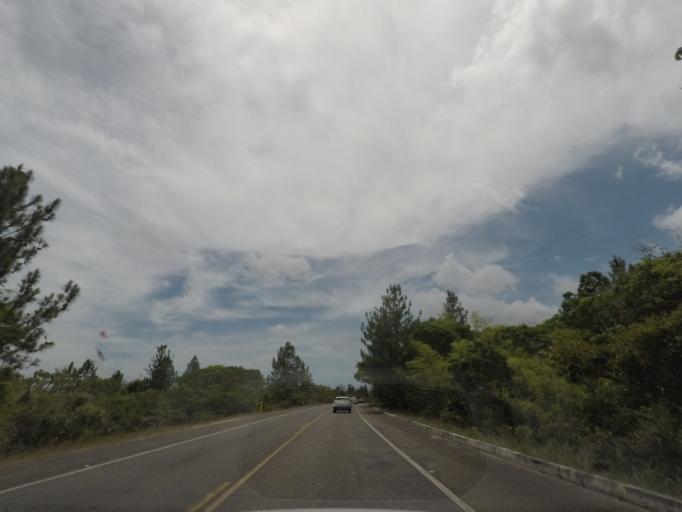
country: BR
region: Bahia
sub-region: Entre Rios
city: Entre Rios
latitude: -12.1410
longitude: -37.7918
